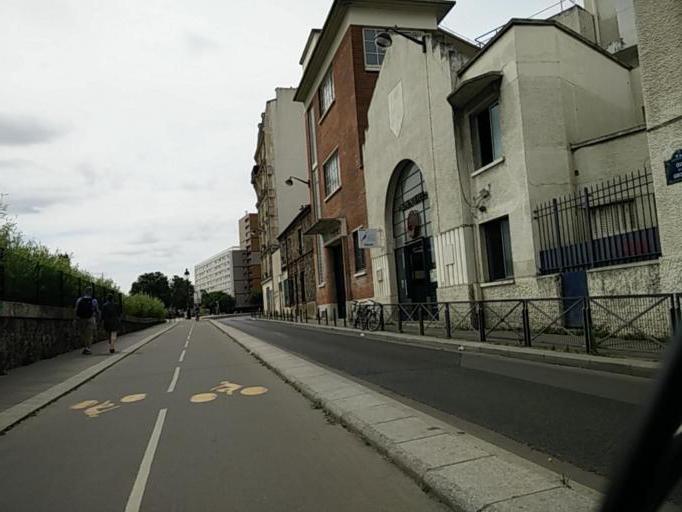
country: FR
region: Ile-de-France
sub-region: Departement de Seine-Saint-Denis
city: Le Pre-Saint-Gervais
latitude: 48.8932
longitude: 2.3852
